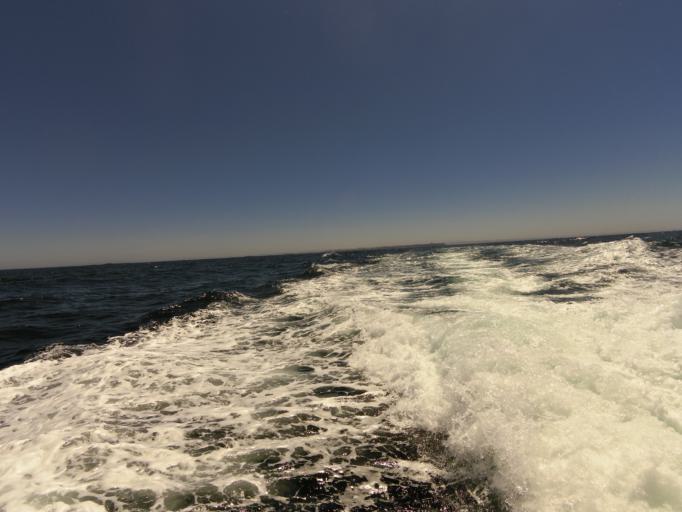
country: PT
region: Leiria
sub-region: Peniche
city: Peniche
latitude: 39.3813
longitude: -9.4540
